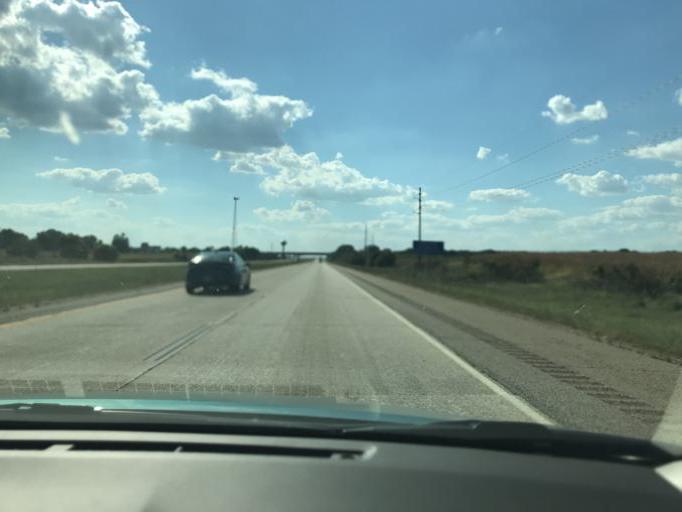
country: US
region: Wisconsin
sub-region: Walworth County
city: Darien
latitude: 42.6151
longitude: -88.7020
